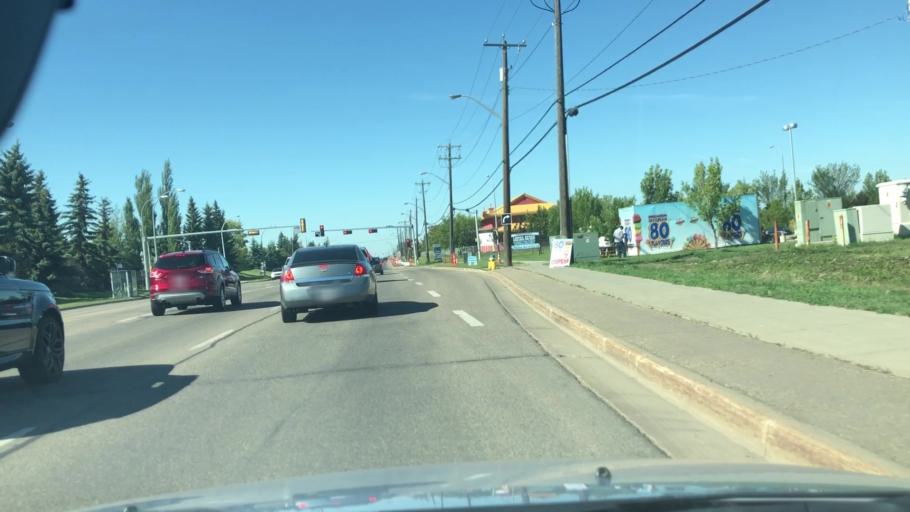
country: CA
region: Alberta
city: Edmonton
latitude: 53.6094
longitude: -113.5412
